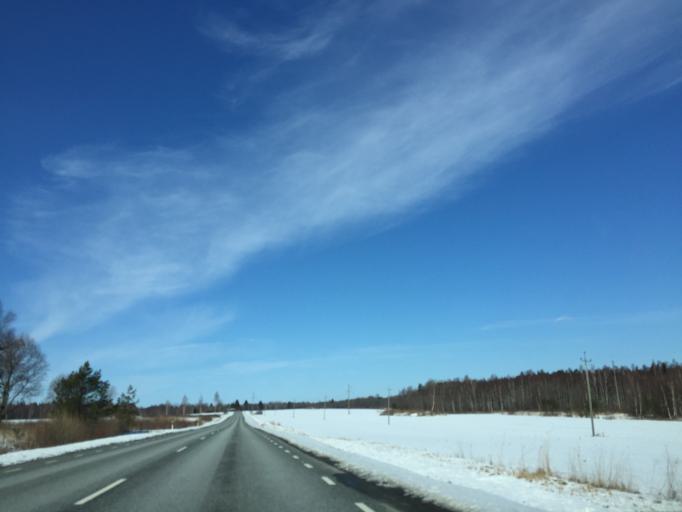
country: EE
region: Laeaene
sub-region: Lihula vald
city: Lihula
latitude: 58.5171
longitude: 24.0845
